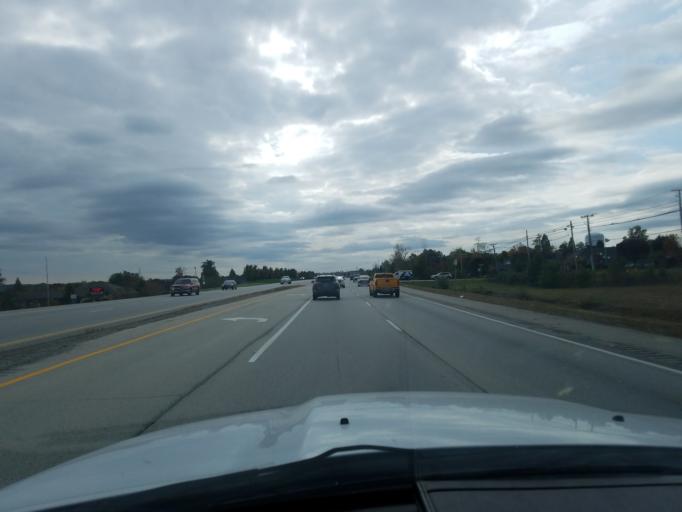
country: US
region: Kentucky
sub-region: Jefferson County
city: Fern Creek
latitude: 38.1290
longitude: -85.5765
